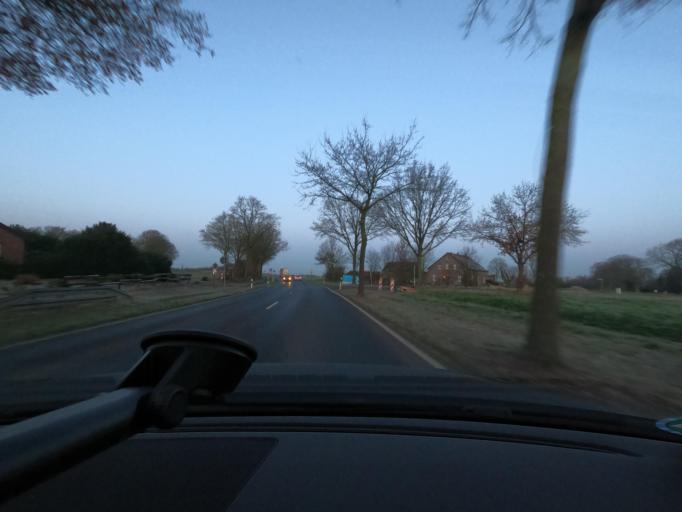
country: DE
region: North Rhine-Westphalia
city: Tonisvorst
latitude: 51.3285
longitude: 6.4660
